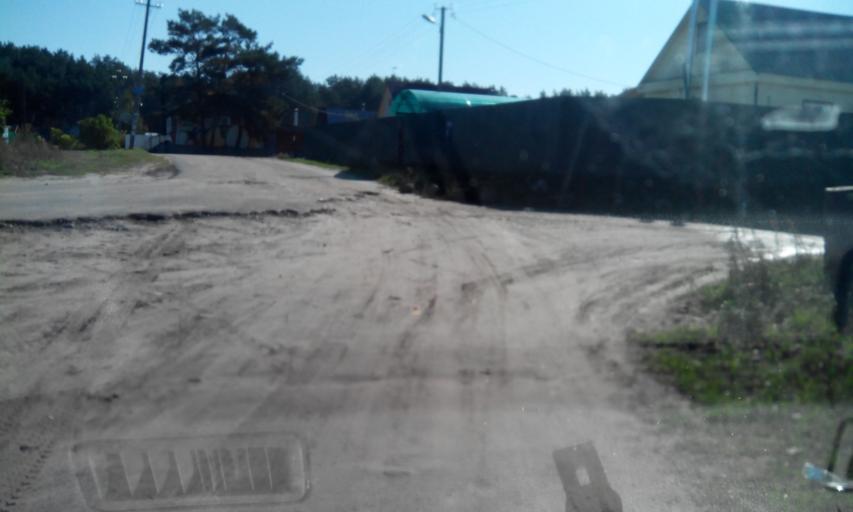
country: RU
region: Penza
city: Zarechnyy
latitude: 53.2729
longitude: 45.1285
